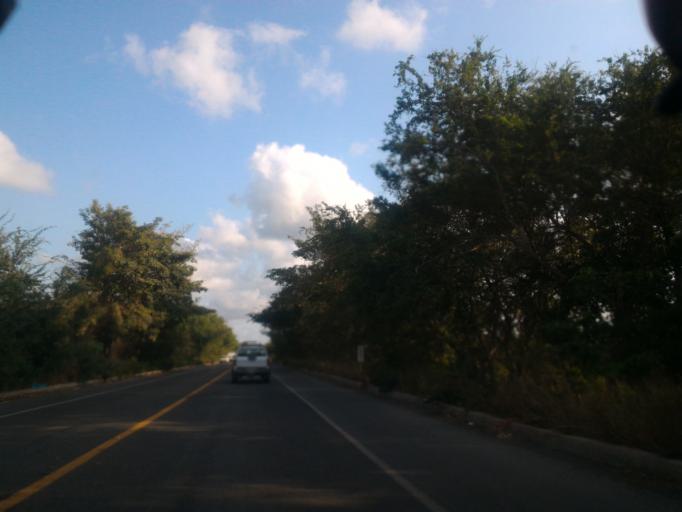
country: MX
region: Colima
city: Tecoman
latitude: 18.8594
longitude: -103.8346
